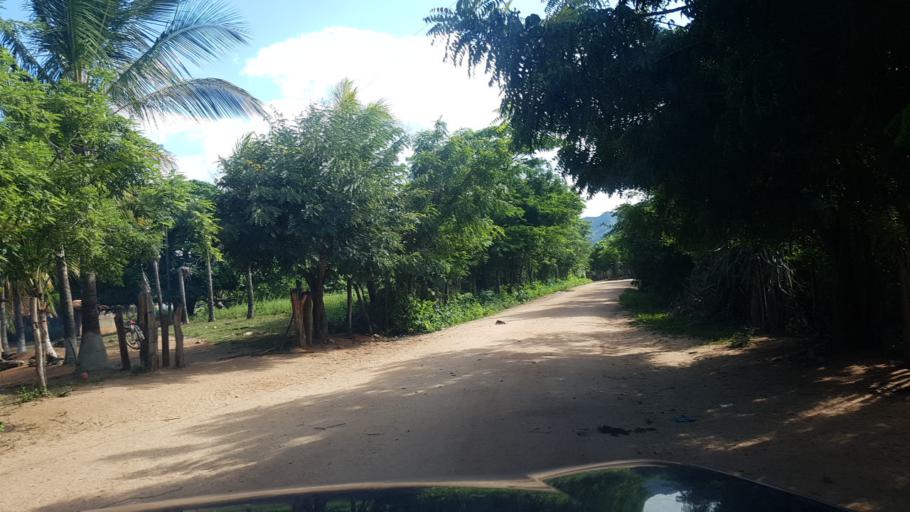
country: NI
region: Nueva Segovia
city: Mozonte
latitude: 13.6561
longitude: -86.3979
